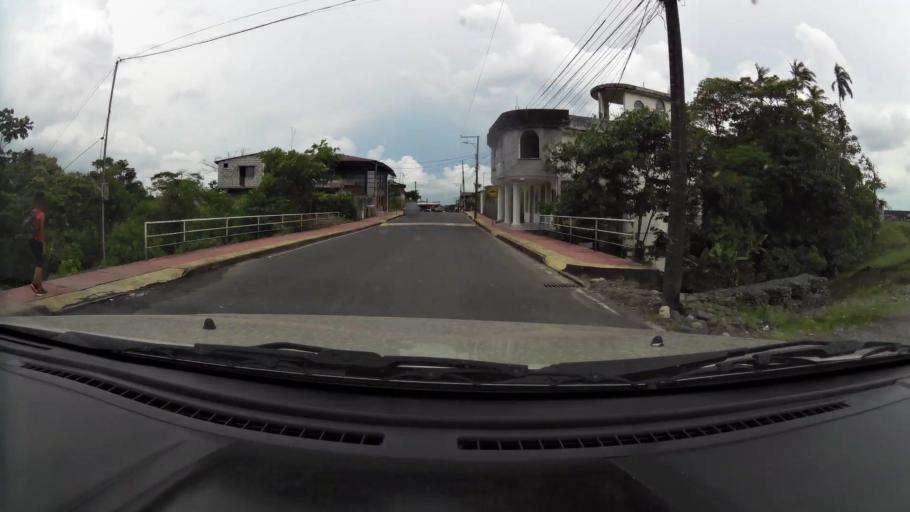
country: EC
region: Pastaza
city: Puyo
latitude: -1.4908
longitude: -78.0020
